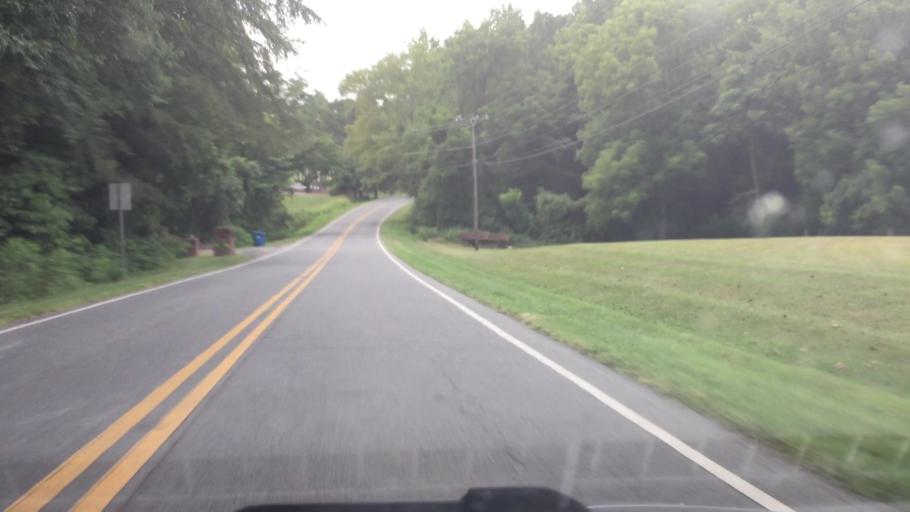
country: US
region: North Carolina
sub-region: Rowan County
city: Enochville
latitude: 35.4680
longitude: -80.7300
